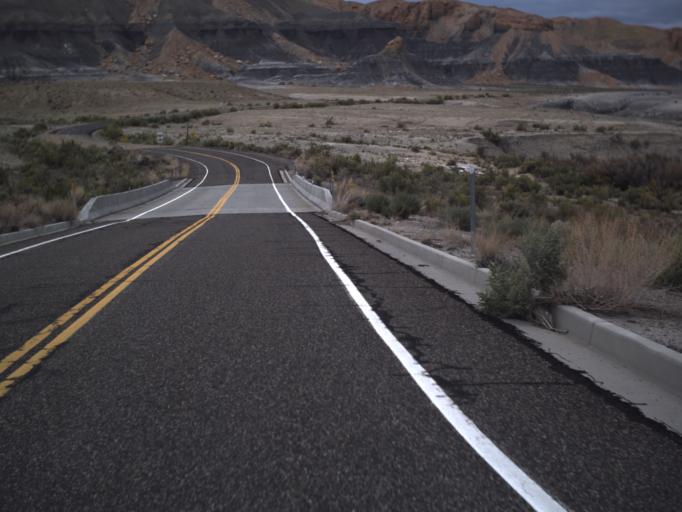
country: US
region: Utah
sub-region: Emery County
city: Ferron
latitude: 38.8126
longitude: -111.2107
